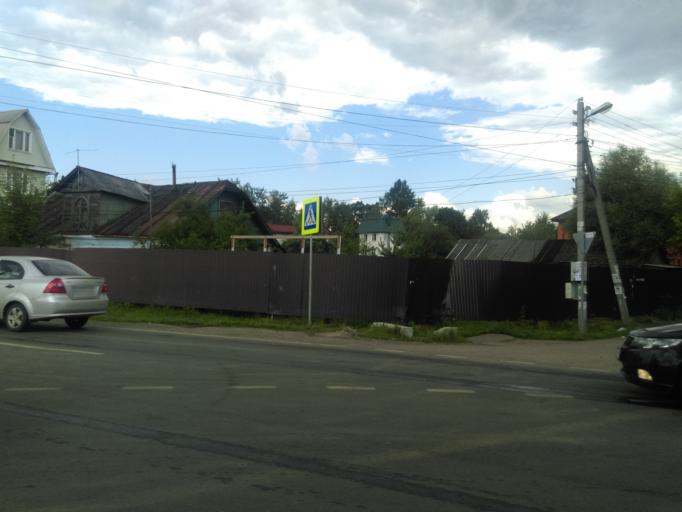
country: RU
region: Moskovskaya
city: Vostryakovo
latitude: 55.3960
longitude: 37.8079
